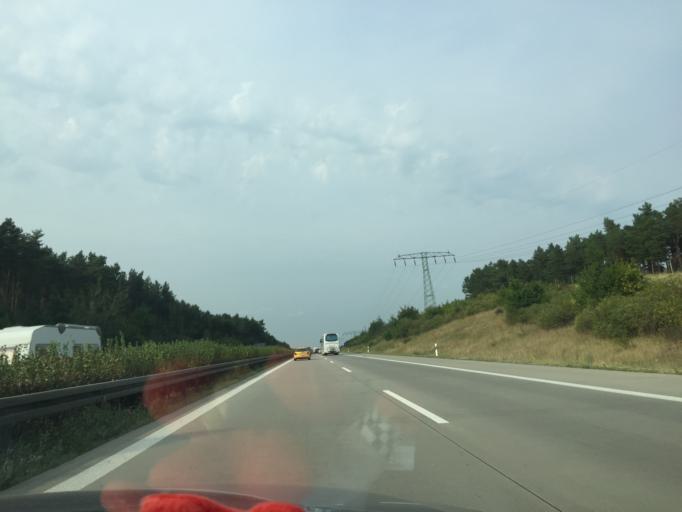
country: DE
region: Brandenburg
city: Schwerin
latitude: 52.1266
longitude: 13.6468
